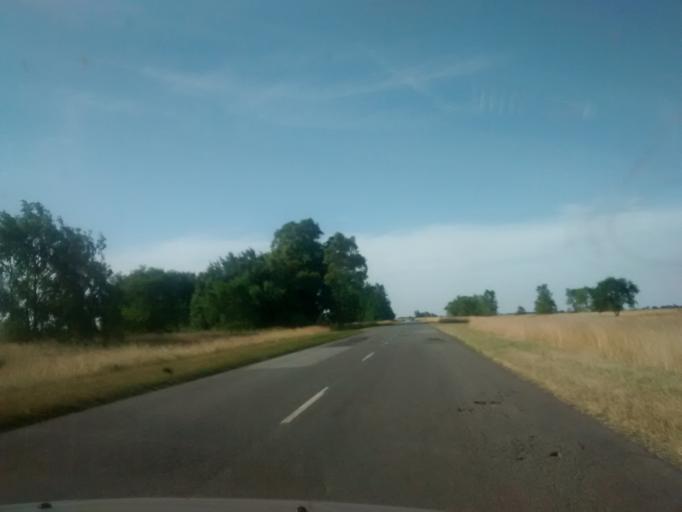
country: AR
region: Buenos Aires
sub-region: Partido de Ayacucho
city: Ayacucho
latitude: -37.4801
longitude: -58.4789
